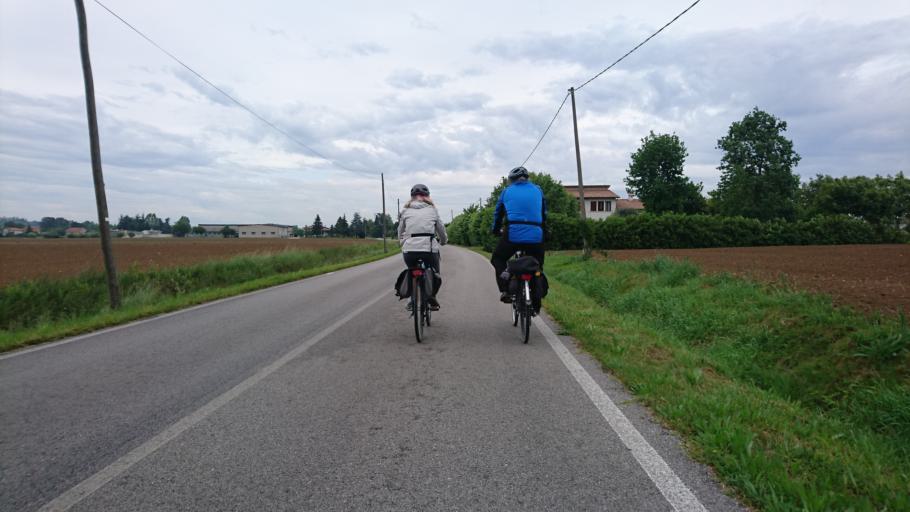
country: IT
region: Veneto
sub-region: Provincia di Padova
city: Cervarese Santa Croce
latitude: 45.4218
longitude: 11.6805
